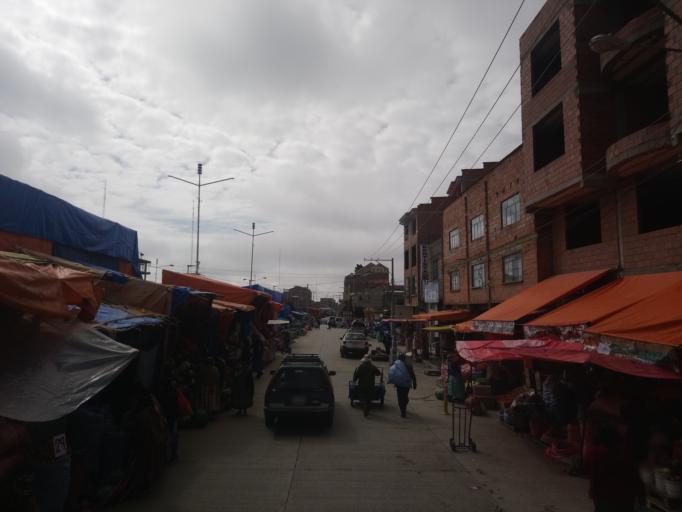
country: BO
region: La Paz
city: La Paz
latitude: -16.5084
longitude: -68.1562
